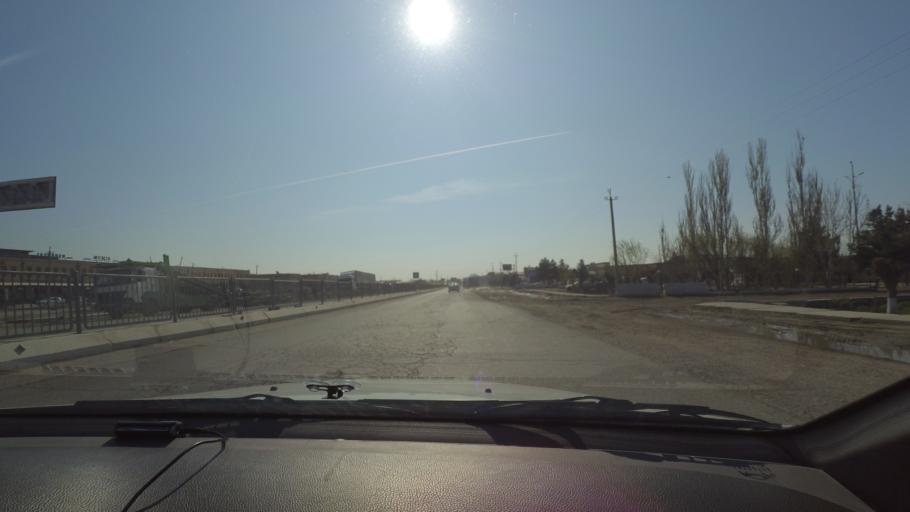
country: UZ
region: Bukhara
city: Bukhara
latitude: 39.8076
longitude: 64.4203
